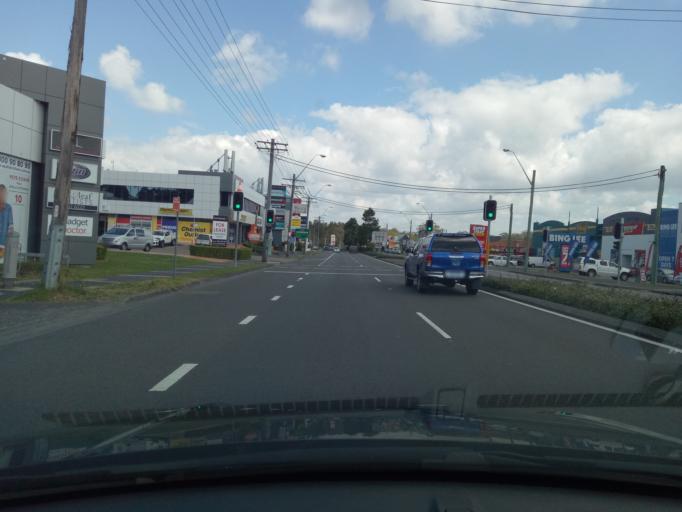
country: AU
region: New South Wales
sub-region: Gosford Shire
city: Erina
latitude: -33.4347
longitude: 151.3878
